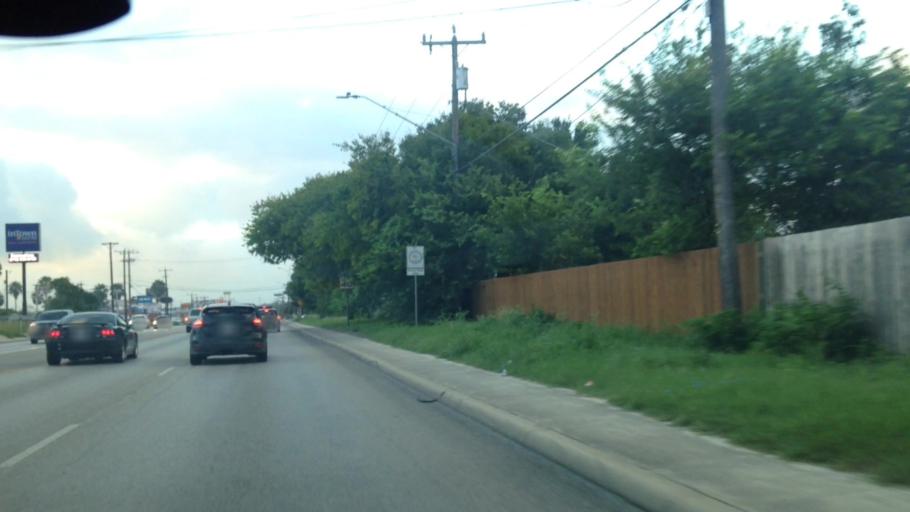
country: US
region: Texas
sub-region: Bexar County
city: Windcrest
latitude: 29.5289
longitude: -98.4111
